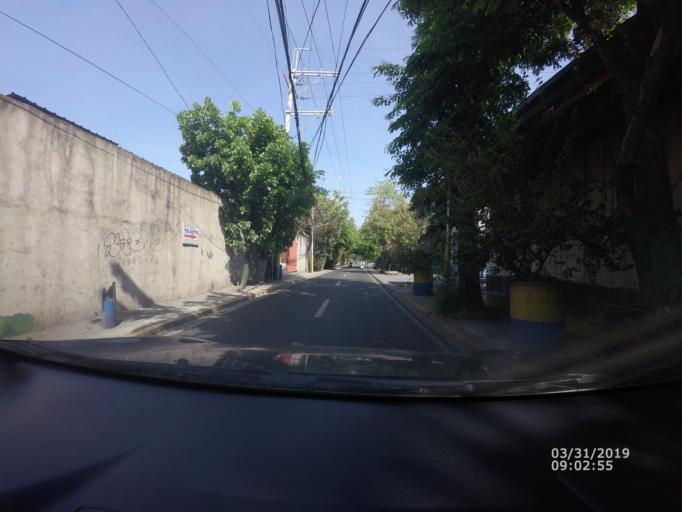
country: PH
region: Metro Manila
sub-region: Mandaluyong
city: Mandaluyong City
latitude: 14.5781
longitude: 121.0217
